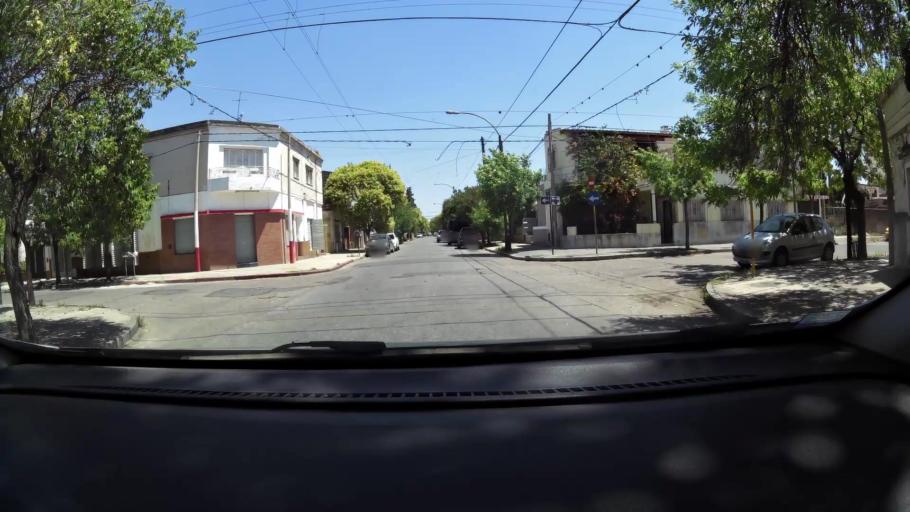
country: AR
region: Cordoba
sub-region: Departamento de Capital
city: Cordoba
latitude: -31.3868
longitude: -64.1589
